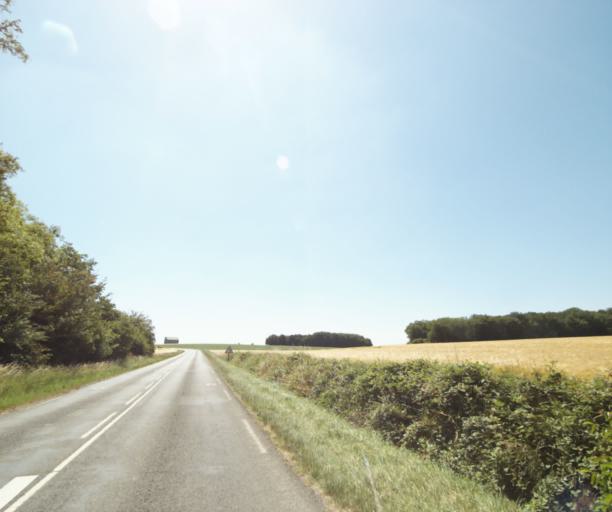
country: FR
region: Ile-de-France
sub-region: Departement de l'Essonne
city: Milly-la-Foret
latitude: 48.3567
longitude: 2.4574
